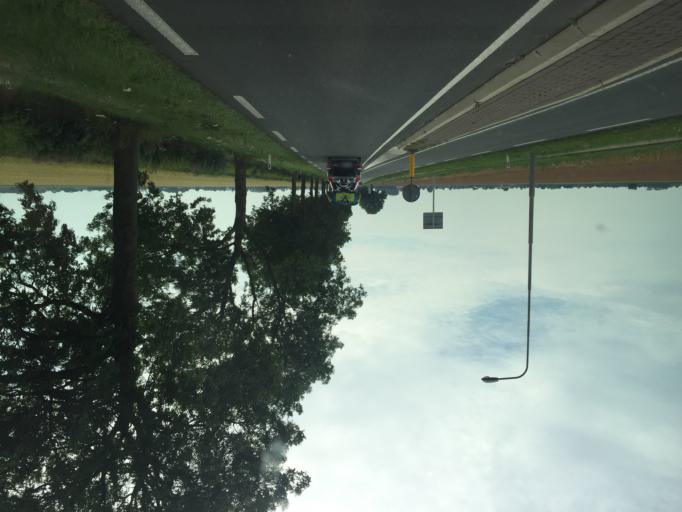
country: NL
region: North Holland
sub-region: Gemeente Beemster
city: Halfweg
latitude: 52.5933
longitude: 4.9124
